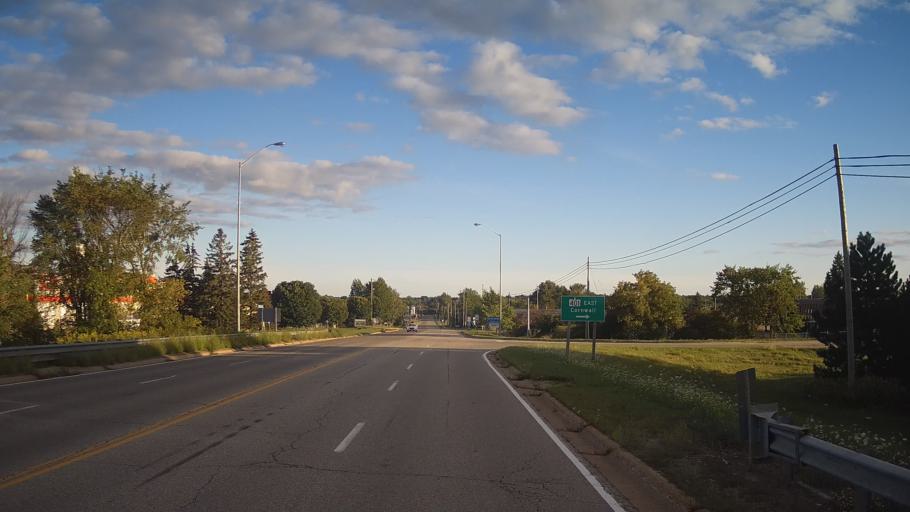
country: CA
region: Ontario
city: Gananoque
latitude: 44.3438
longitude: -76.1713
